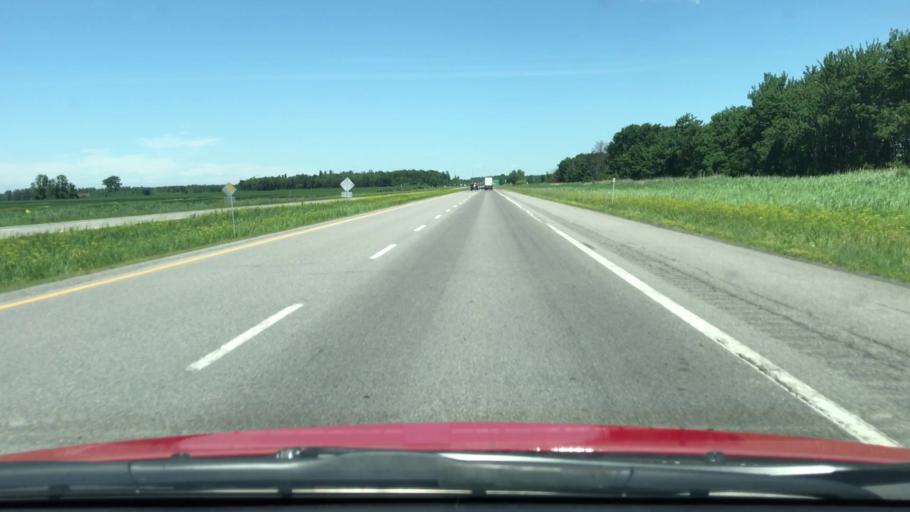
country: CA
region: Quebec
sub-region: Monteregie
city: Napierville
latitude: 45.1755
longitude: -73.4606
